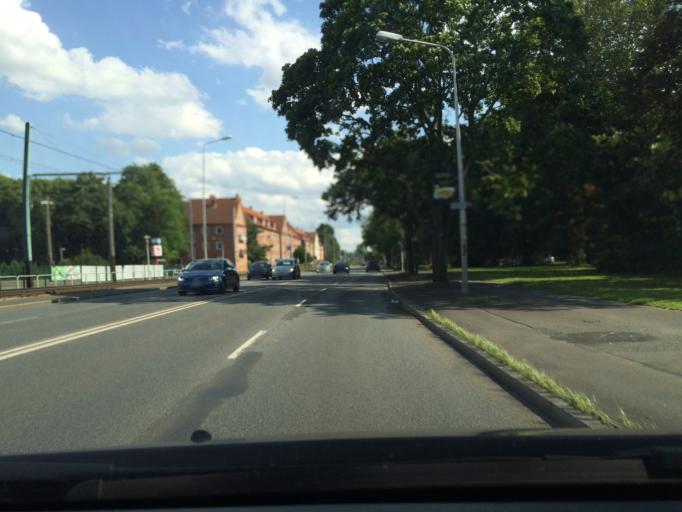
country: DE
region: Mecklenburg-Vorpommern
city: Rostock
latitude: 54.0980
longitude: 12.0904
